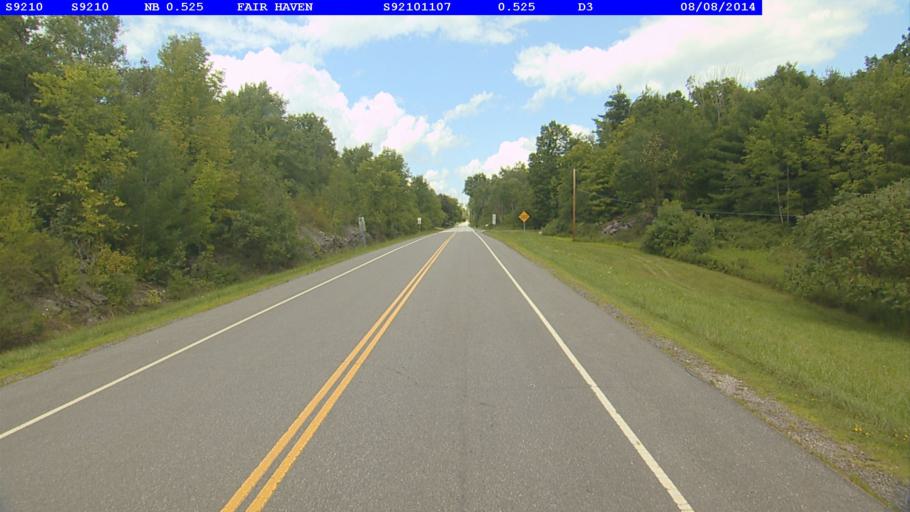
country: US
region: Vermont
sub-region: Rutland County
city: Fair Haven
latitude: 43.6070
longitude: -73.2593
